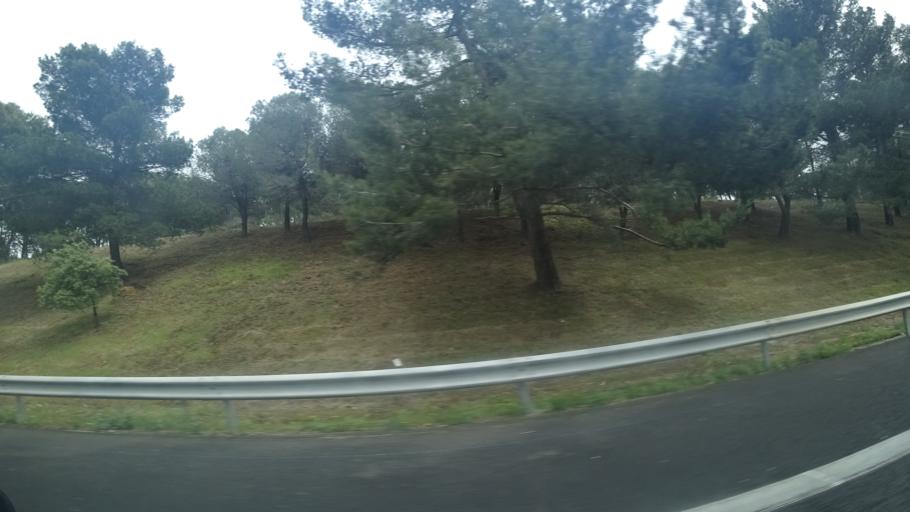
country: FR
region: Languedoc-Roussillon
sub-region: Departement de l'Aude
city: Vinassan
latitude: 43.2009
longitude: 3.0799
